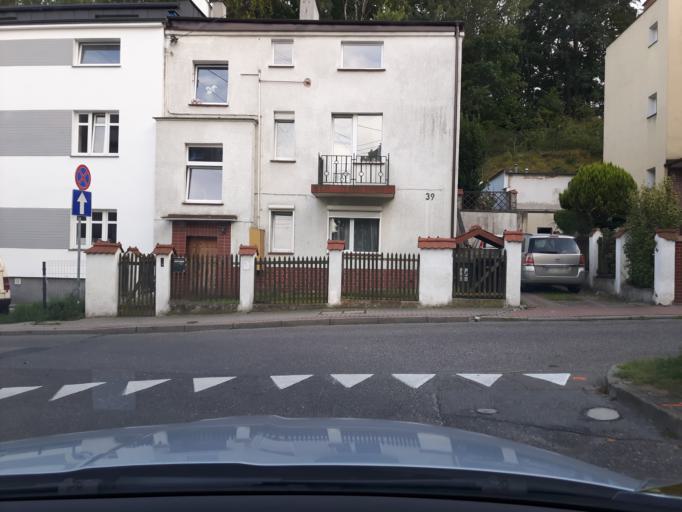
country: PL
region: Pomeranian Voivodeship
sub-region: Gdynia
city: Gdynia
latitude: 54.5130
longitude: 18.5251
